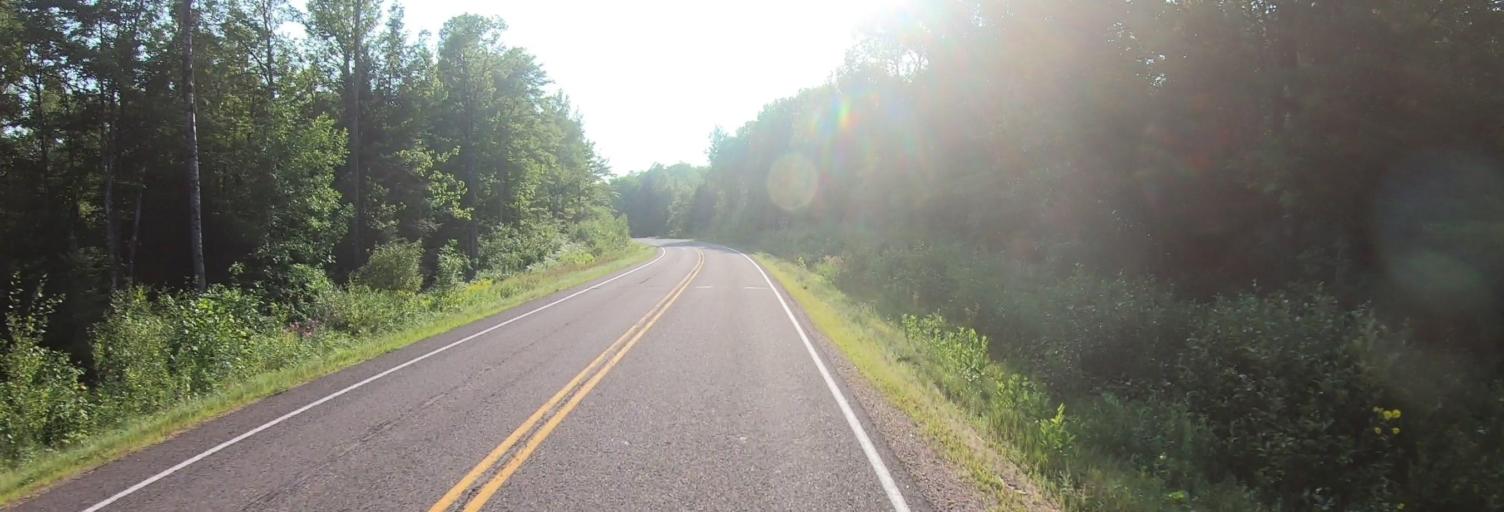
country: US
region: Wisconsin
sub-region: Ashland County
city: Ashland
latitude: 46.3151
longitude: -90.7151
